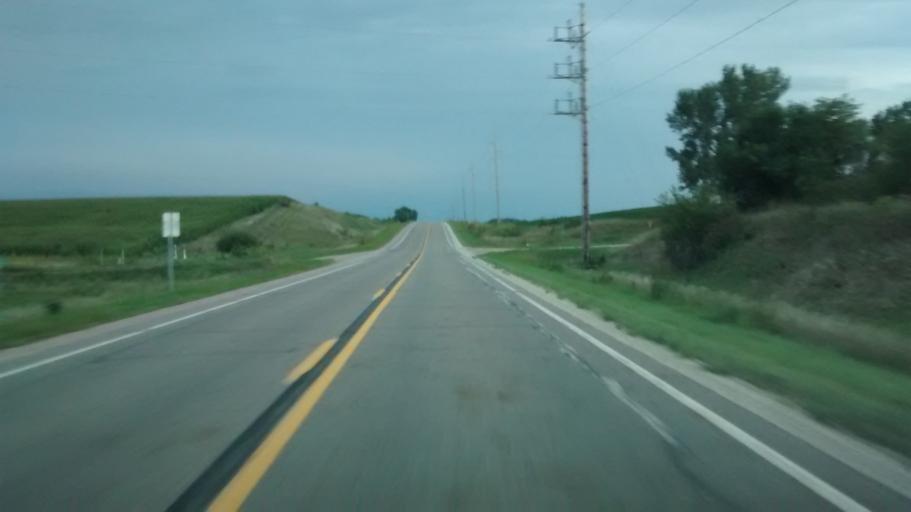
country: US
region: Iowa
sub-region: Woodbury County
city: Moville
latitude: 42.5190
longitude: -96.0476
